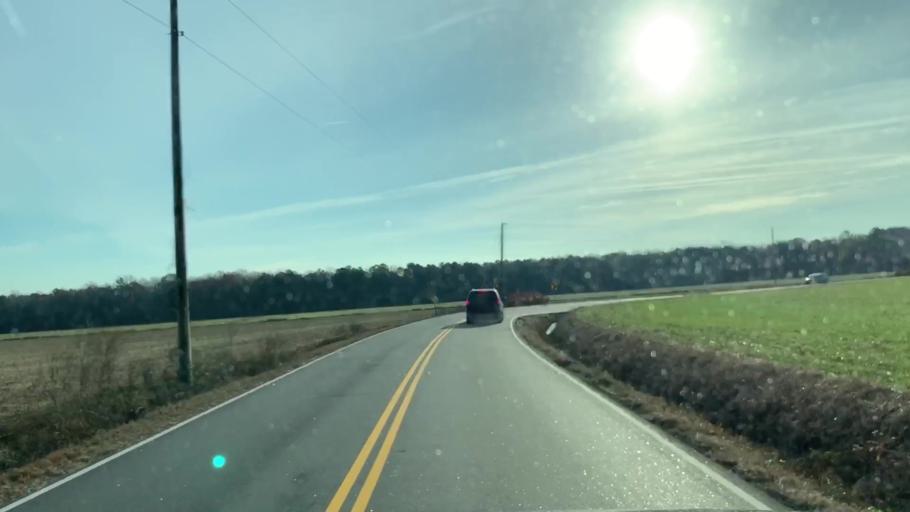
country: US
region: Virginia
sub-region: City of Virginia Beach
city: Virginia Beach
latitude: 36.7174
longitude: -76.0509
